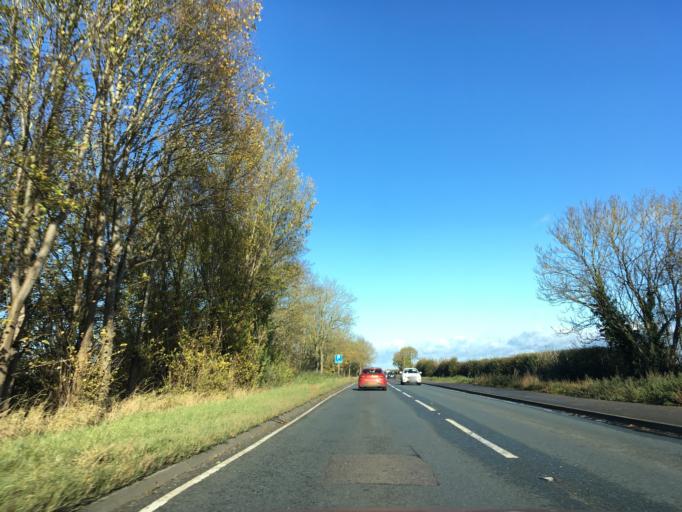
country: GB
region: England
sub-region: Worcestershire
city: Evesham
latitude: 52.0642
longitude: -1.9562
